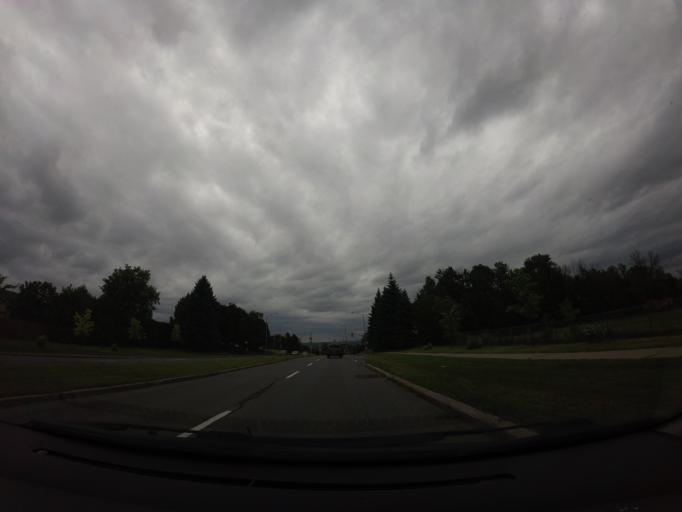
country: CA
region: Quebec
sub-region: Outaouais
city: Gatineau
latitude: 45.4645
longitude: -75.5276
